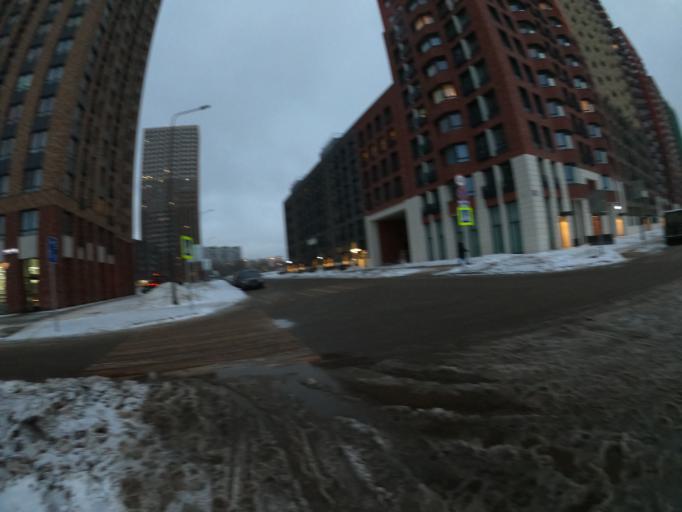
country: RU
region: Moskovskaya
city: Kur'yanovo
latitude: 55.6461
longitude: 37.7042
